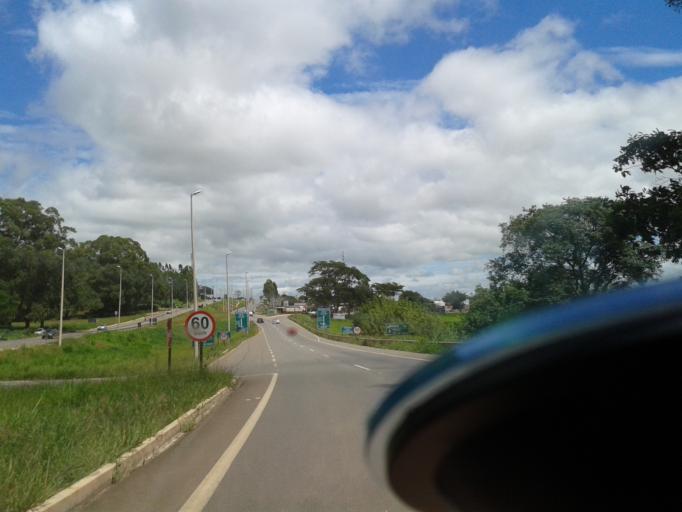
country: BR
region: Goias
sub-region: Inhumas
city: Inhumas
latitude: -16.3923
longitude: -49.4943
